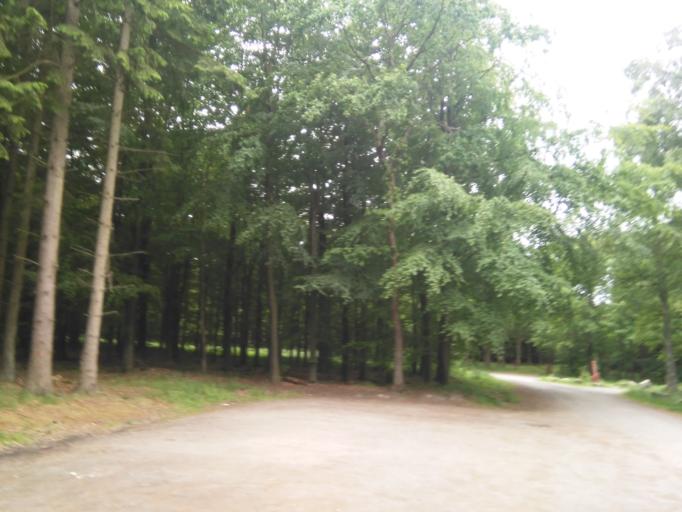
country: DK
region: Capital Region
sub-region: Bornholm Kommune
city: Akirkeby
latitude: 55.1129
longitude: 14.9401
